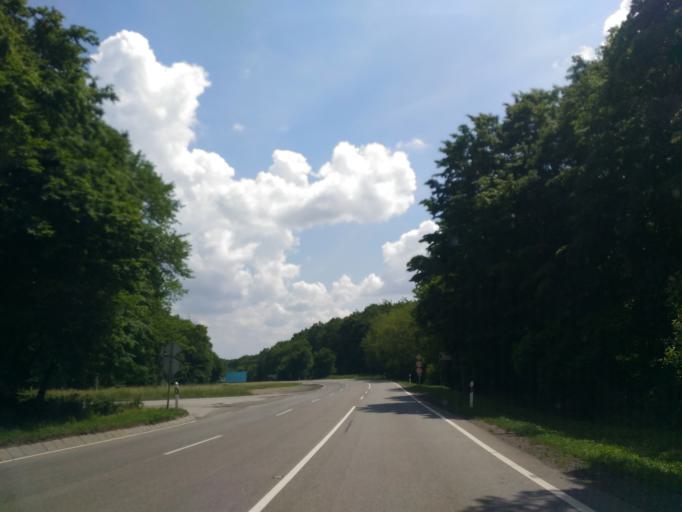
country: HU
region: Baranya
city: Pecs
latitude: 46.1315
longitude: 18.2521
